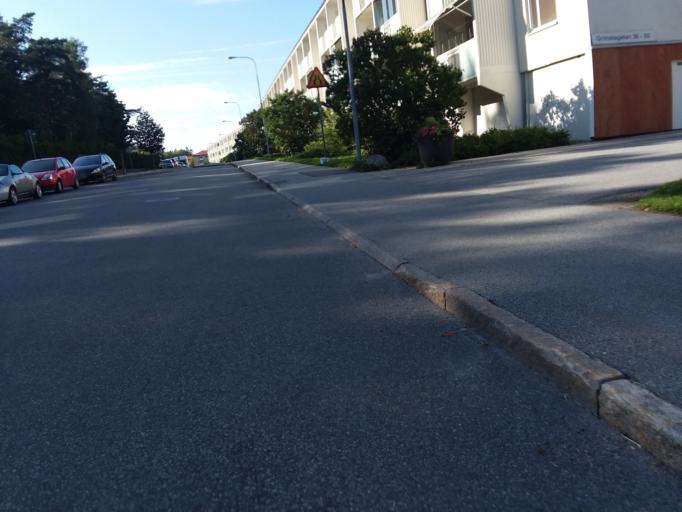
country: SE
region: Stockholm
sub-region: Stockholms Kommun
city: Bromma
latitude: 59.3547
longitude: 17.8754
